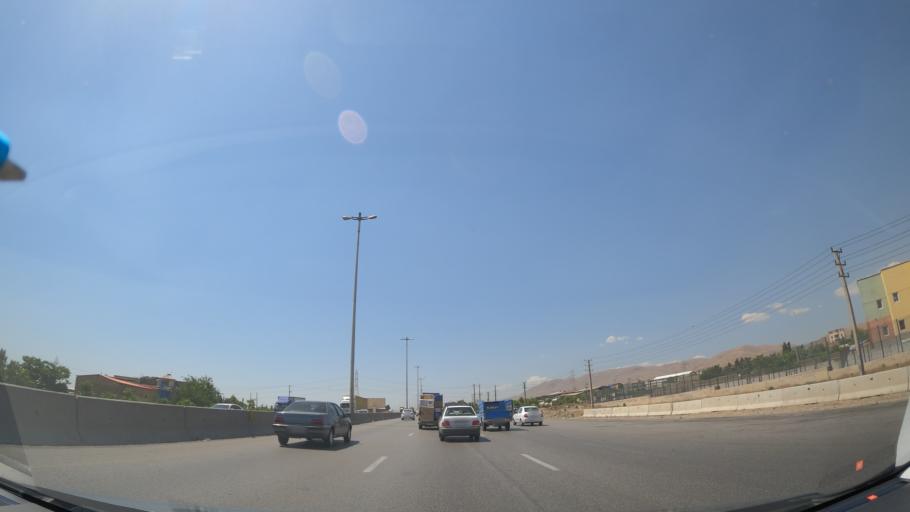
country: IR
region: Alborz
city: Karaj
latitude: 35.8682
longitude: 50.9002
